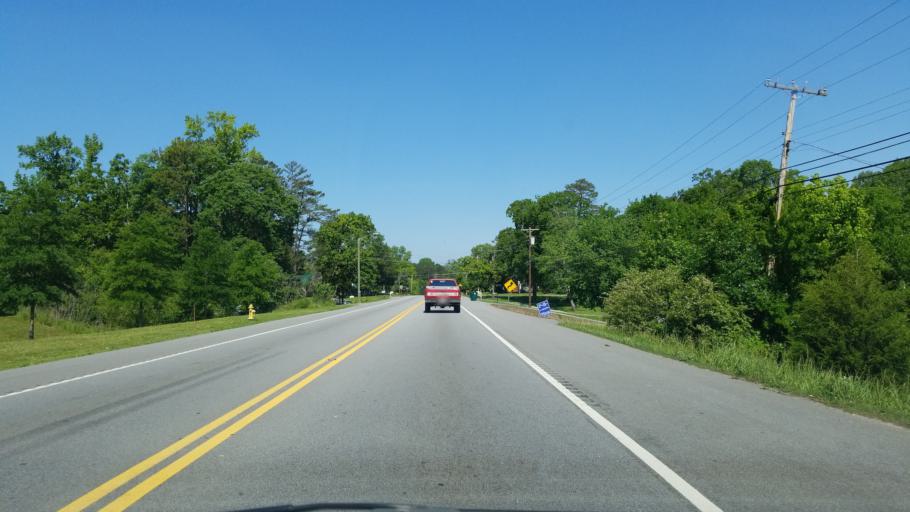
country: US
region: Tennessee
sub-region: Hamilton County
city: Harrison
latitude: 35.0638
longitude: -85.1413
